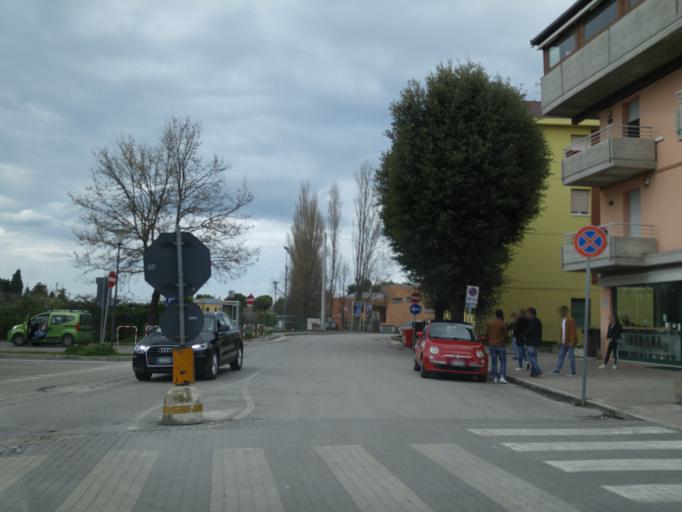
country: IT
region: The Marches
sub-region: Provincia di Pesaro e Urbino
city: Fano
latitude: 43.8429
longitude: 13.0084
